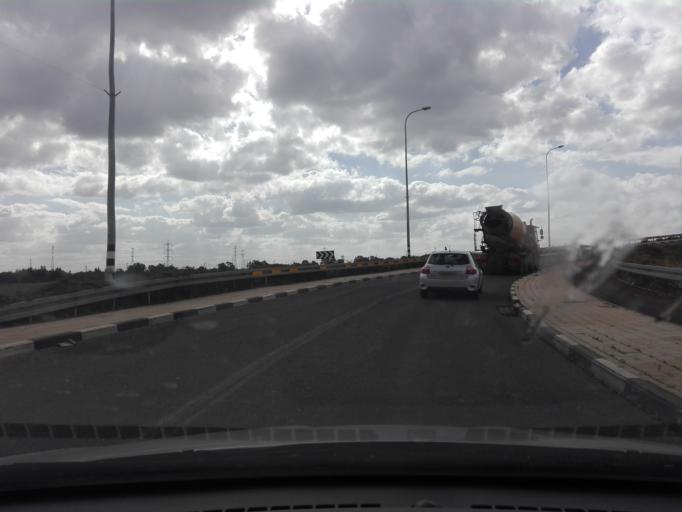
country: IL
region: Haifa
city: Qesarya
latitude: 32.5108
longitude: 34.9529
